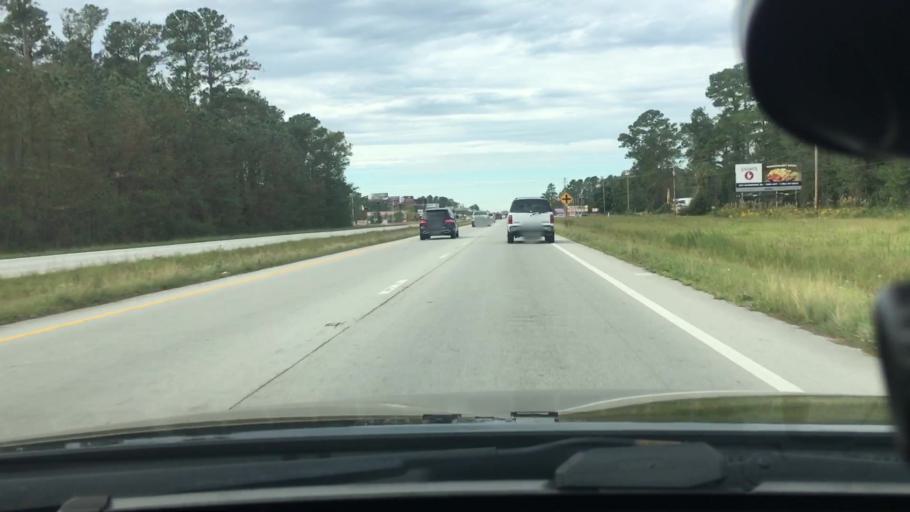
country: US
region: North Carolina
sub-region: Craven County
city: James City
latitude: 35.0539
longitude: -77.0163
